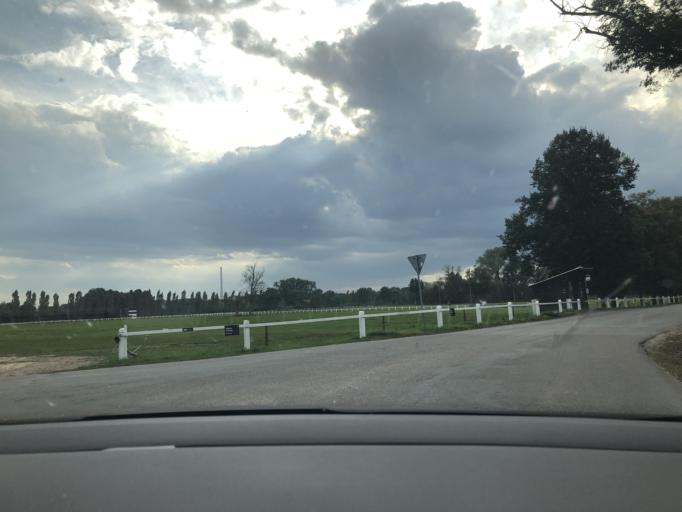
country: CZ
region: Pardubicky
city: Recany nad Labem
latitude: 50.0573
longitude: 15.4823
